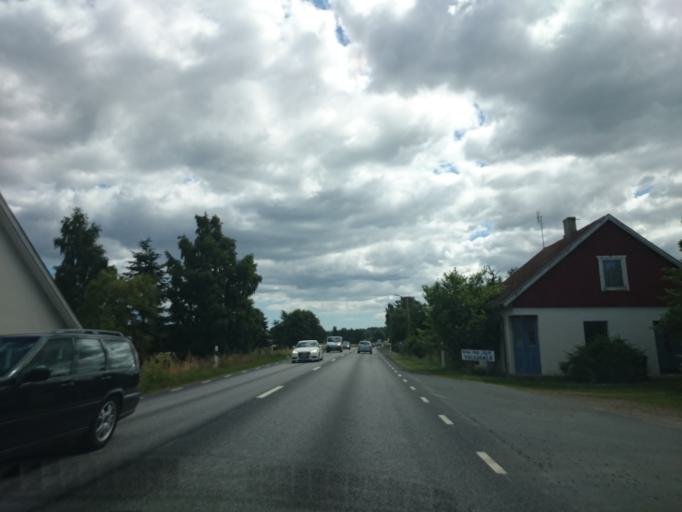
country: SE
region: Skane
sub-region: Kristianstads Kommun
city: Degeberga
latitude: 55.8136
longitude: 14.1348
